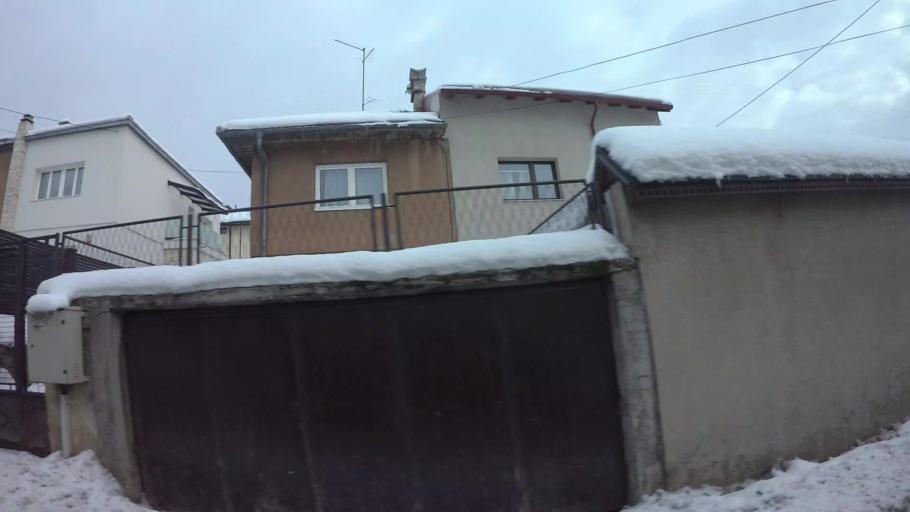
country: BA
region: Federation of Bosnia and Herzegovina
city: Kobilja Glava
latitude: 43.8666
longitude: 18.4329
